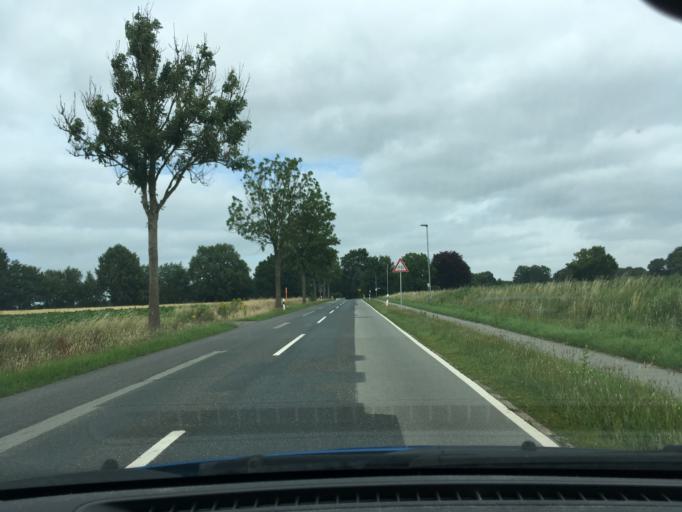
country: DE
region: Lower Saxony
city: Buchholz in der Nordheide
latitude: 53.3651
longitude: 9.9020
